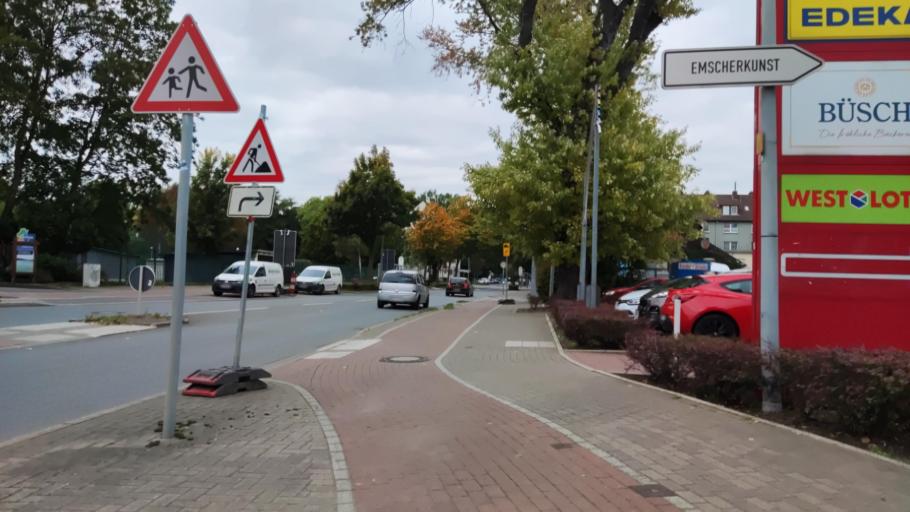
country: DE
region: North Rhine-Westphalia
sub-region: Regierungsbezirk Arnsberg
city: Herne
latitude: 51.5573
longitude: 7.2302
